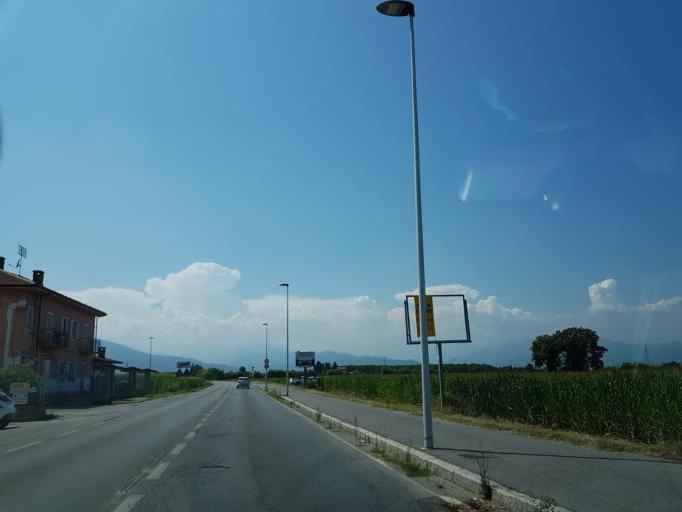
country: IT
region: Piedmont
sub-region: Provincia di Cuneo
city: San Defendente
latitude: 44.3945
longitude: 7.5169
